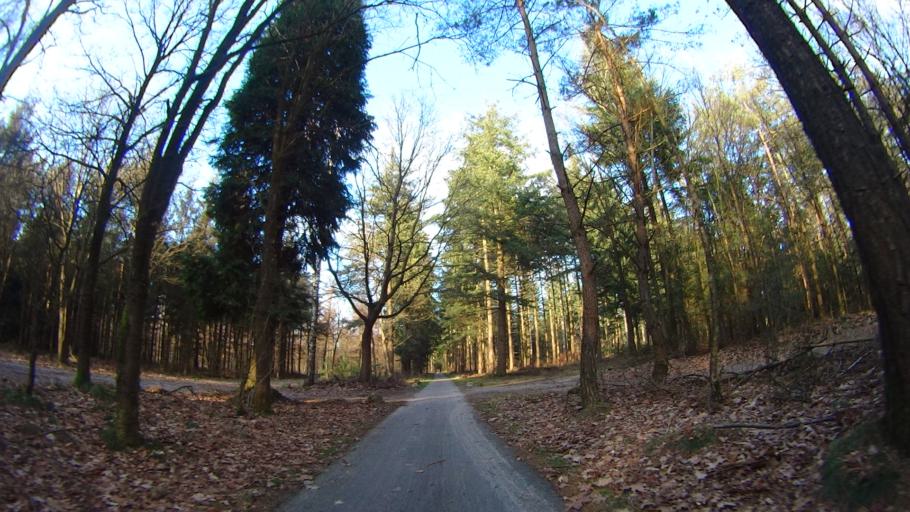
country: NL
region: Drenthe
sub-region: Gemeente Coevorden
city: Sleen
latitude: 52.8081
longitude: 6.7701
